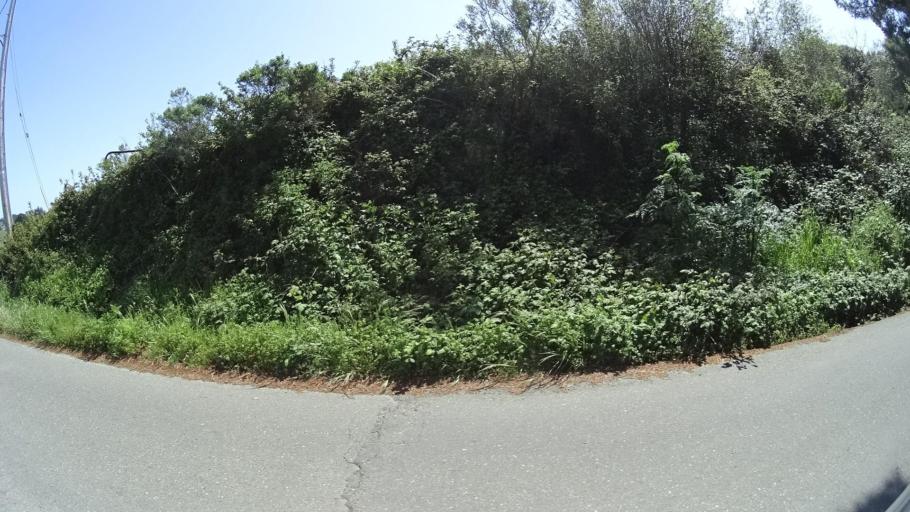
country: US
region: California
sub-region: Humboldt County
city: Fortuna
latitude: 40.5630
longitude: -124.1386
